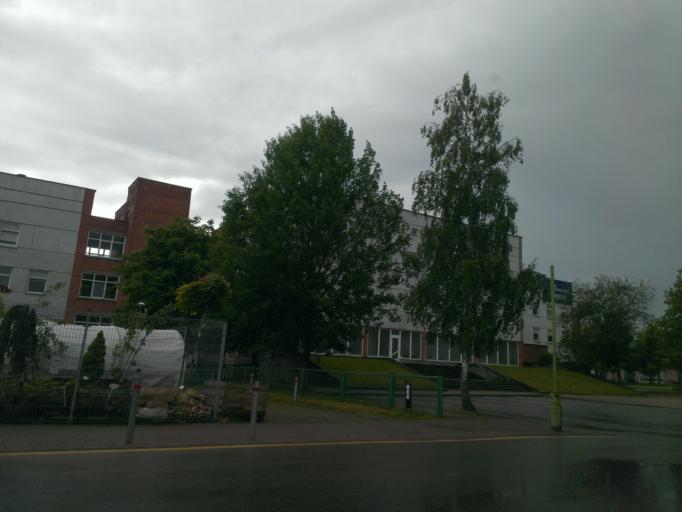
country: LT
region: Klaipedos apskritis
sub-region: Klaipeda
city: Klaipeda
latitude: 55.7520
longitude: 21.1299
